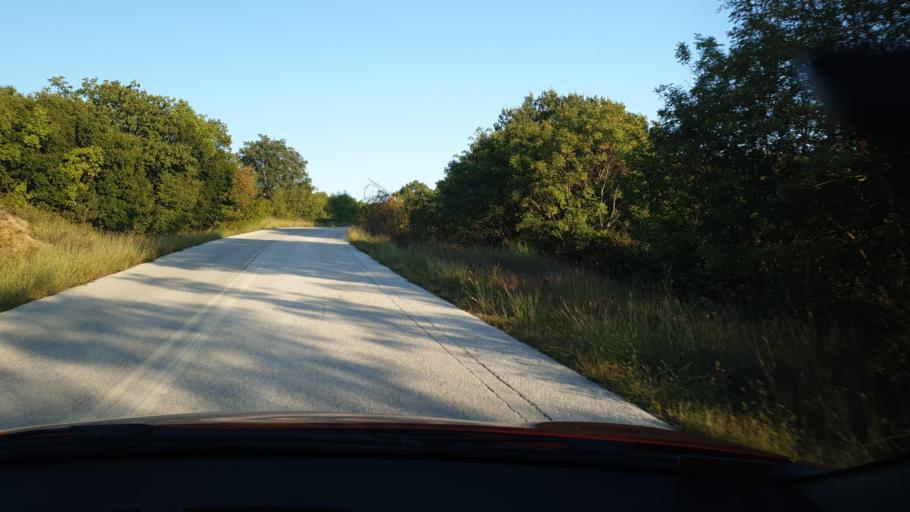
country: GR
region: Central Macedonia
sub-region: Nomos Chalkidikis
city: Galatista
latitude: 40.5487
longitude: 23.2826
